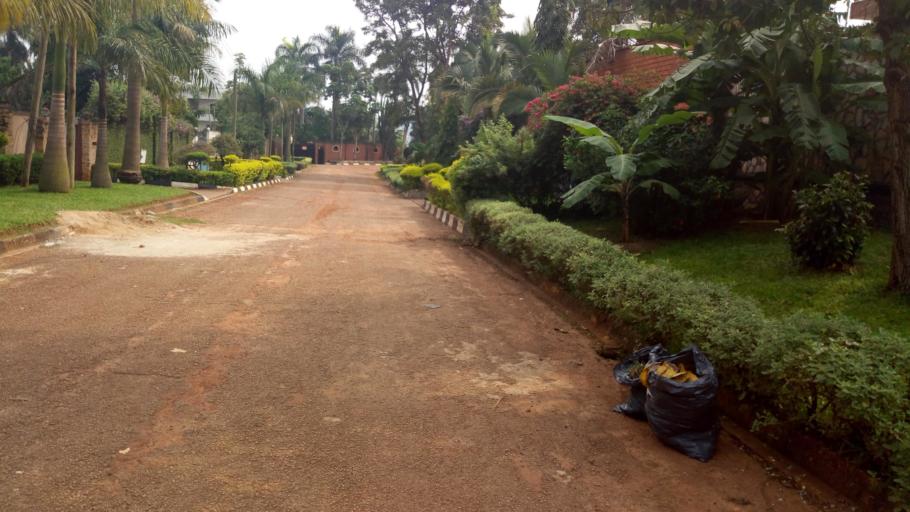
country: UG
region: Central Region
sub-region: Kampala District
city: Kampala
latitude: 0.3092
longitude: 32.6242
